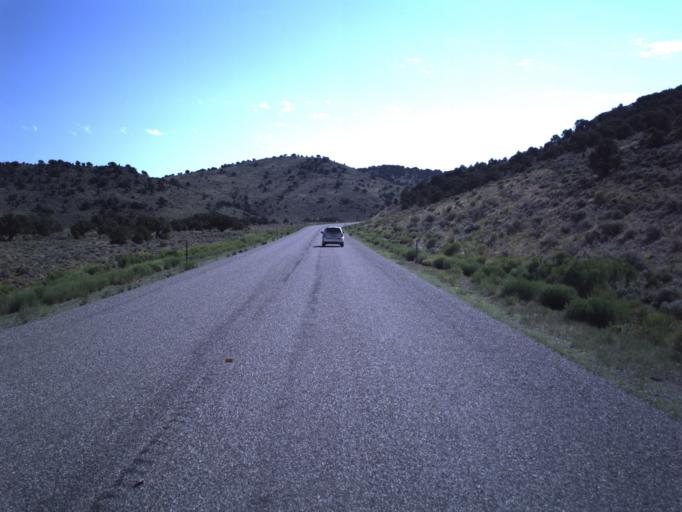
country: US
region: Utah
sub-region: Wayne County
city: Loa
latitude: 38.4773
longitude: -111.5687
